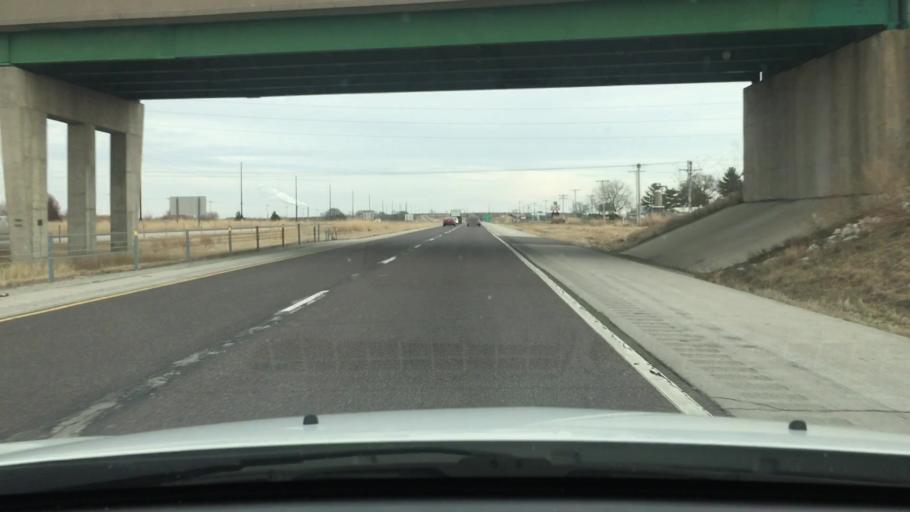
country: US
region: Illinois
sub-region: Sangamon County
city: Jerome
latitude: 39.7418
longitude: -89.6876
